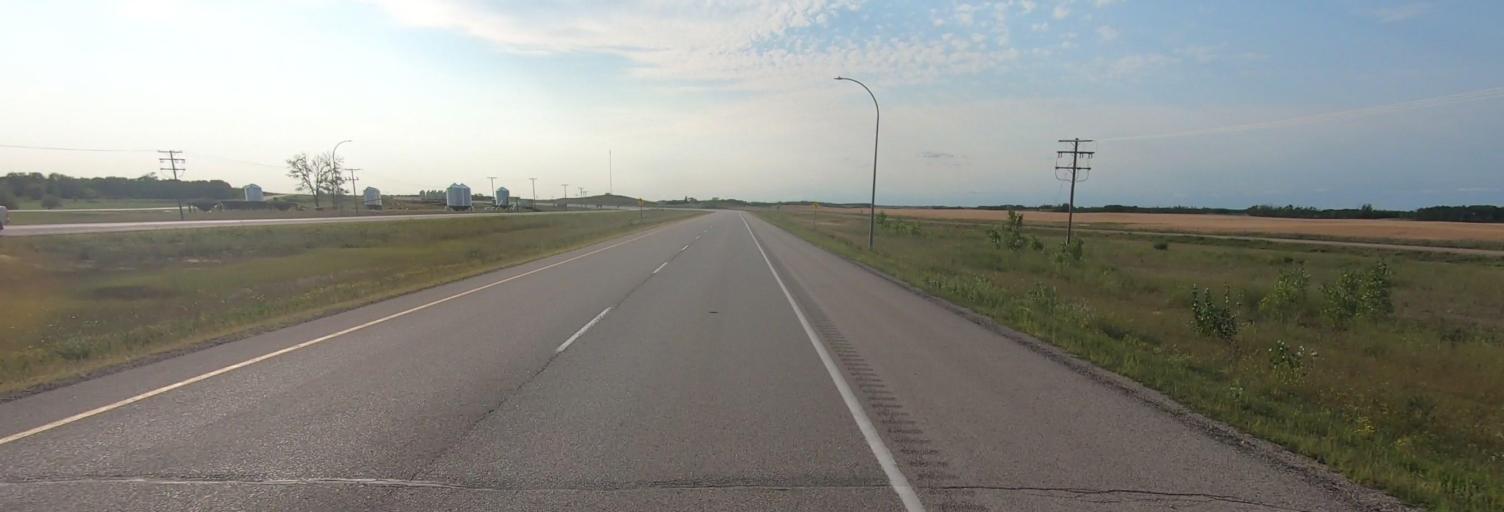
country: CA
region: Saskatchewan
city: Esterhazy
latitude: 50.3841
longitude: -102.5826
